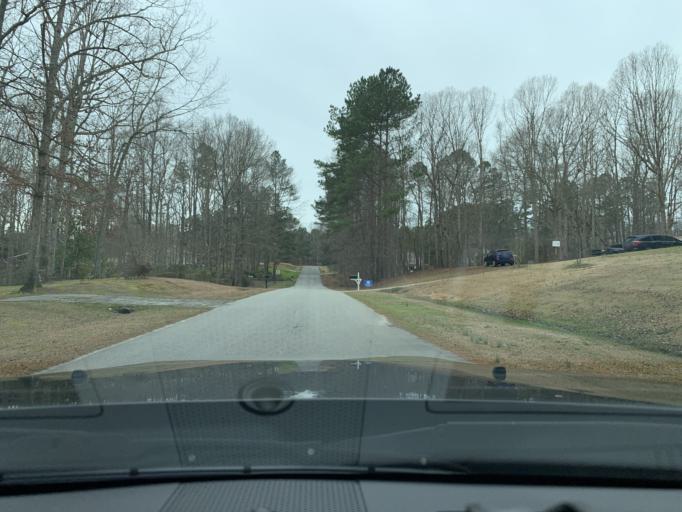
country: US
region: North Carolina
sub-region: Johnston County
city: Wilsons Mills
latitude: 35.6227
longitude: -78.3910
